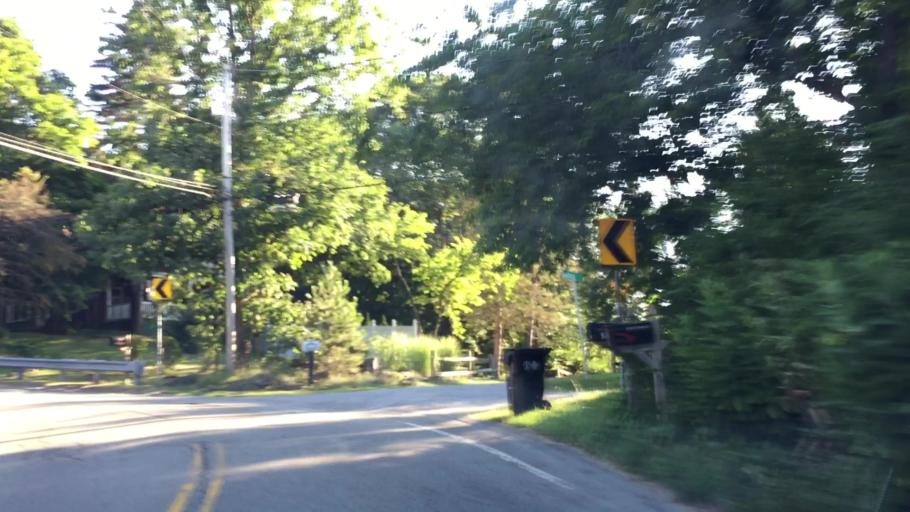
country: US
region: Pennsylvania
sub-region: Allegheny County
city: Franklin Park
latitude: 40.5874
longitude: -80.0546
